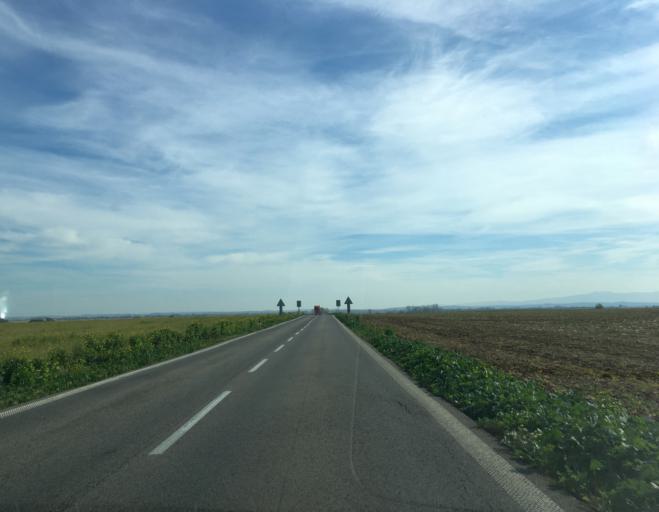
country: SK
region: Nitriansky
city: Zeliezovce
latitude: 48.0972
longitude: 18.5662
